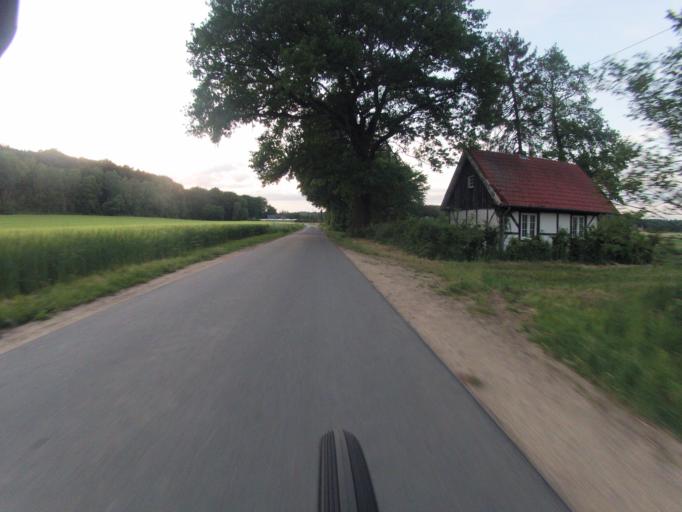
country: DE
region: North Rhine-Westphalia
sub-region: Regierungsbezirk Munster
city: Tecklenburg
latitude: 52.2540
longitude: 7.8112
